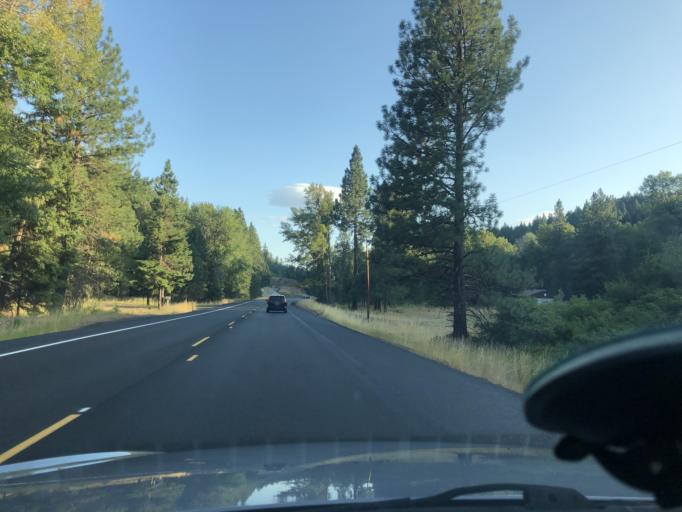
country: US
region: Washington
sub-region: Kittitas County
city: Cle Elum
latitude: 47.2350
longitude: -120.6950
